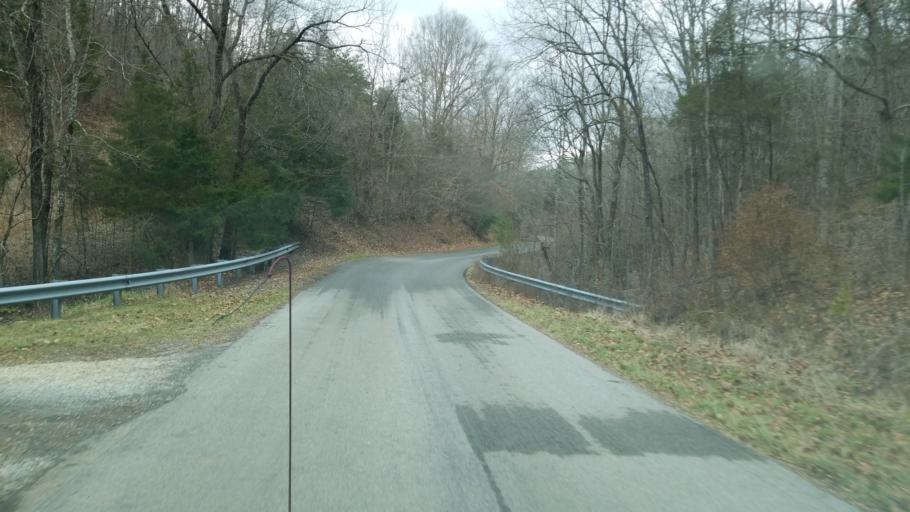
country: US
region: Virginia
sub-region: Giles County
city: Pearisburg
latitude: 37.2323
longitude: -80.6997
